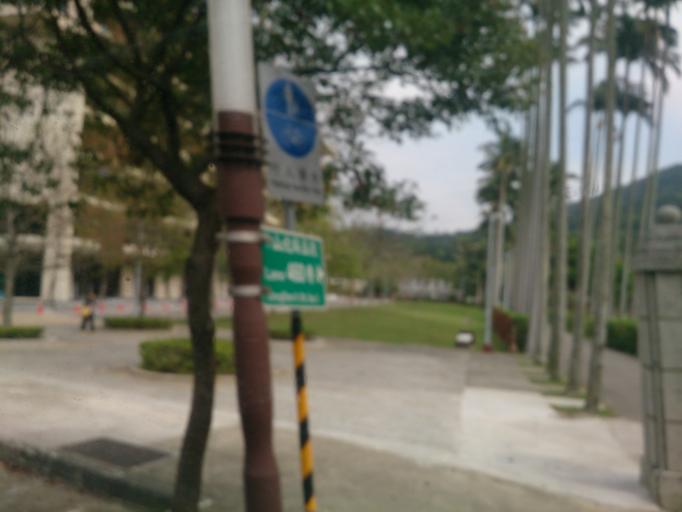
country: TW
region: Taipei
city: Taipei
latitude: 25.0921
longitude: 121.5279
